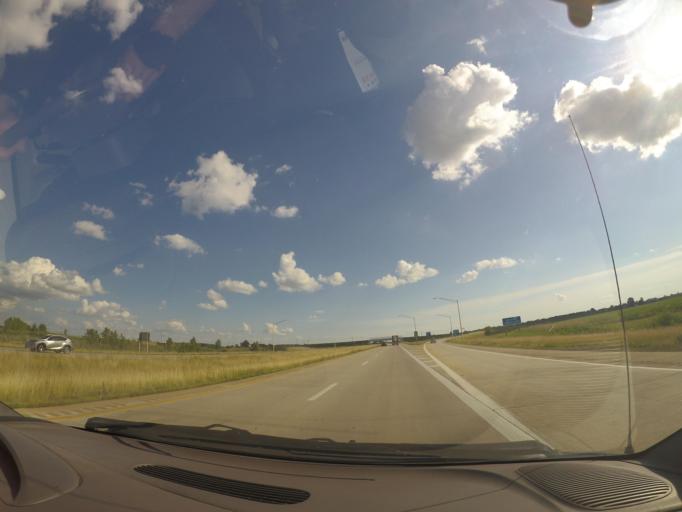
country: US
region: Ohio
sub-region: Lucas County
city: Waterville
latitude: 41.5126
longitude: -83.7522
